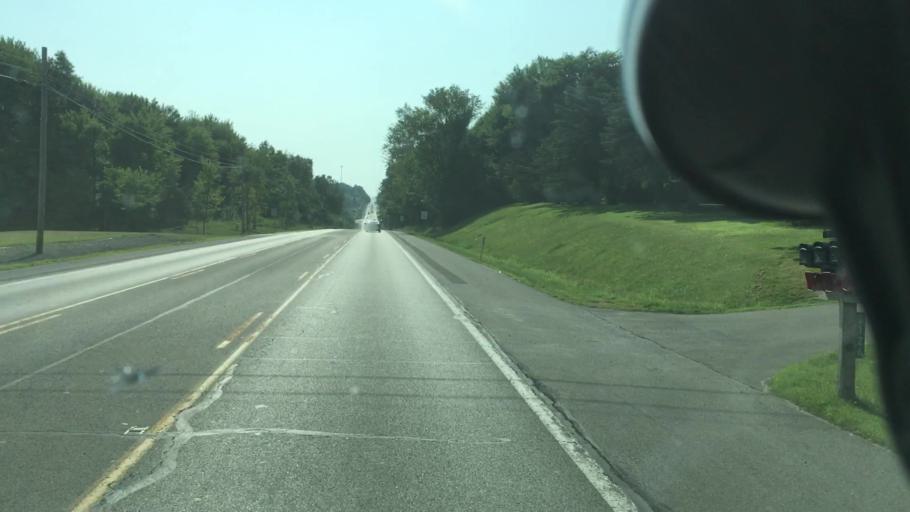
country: US
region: Pennsylvania
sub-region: Lawrence County
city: New Castle
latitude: 40.9752
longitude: -80.2756
